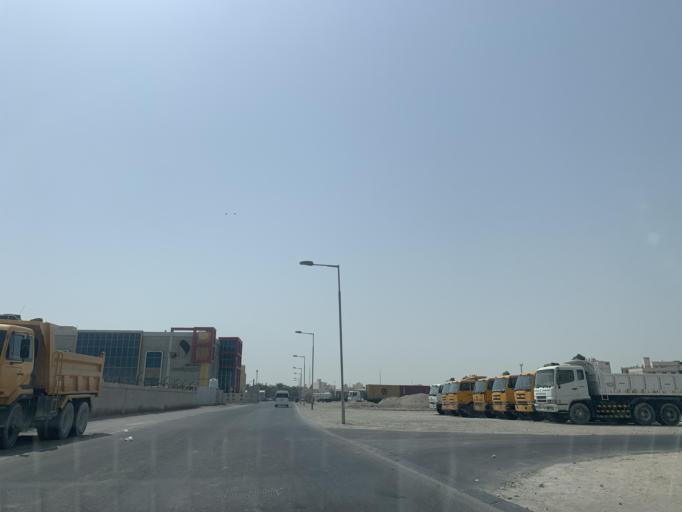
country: BH
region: Northern
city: Madinat `Isa
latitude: 26.1879
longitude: 50.5535
